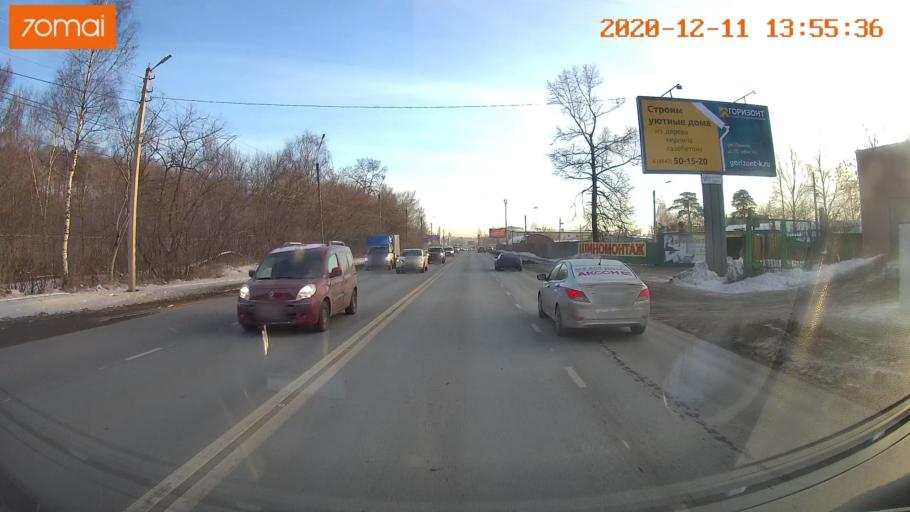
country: RU
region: Kostroma
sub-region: Kostromskoy Rayon
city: Kostroma
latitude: 57.7811
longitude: 40.9661
